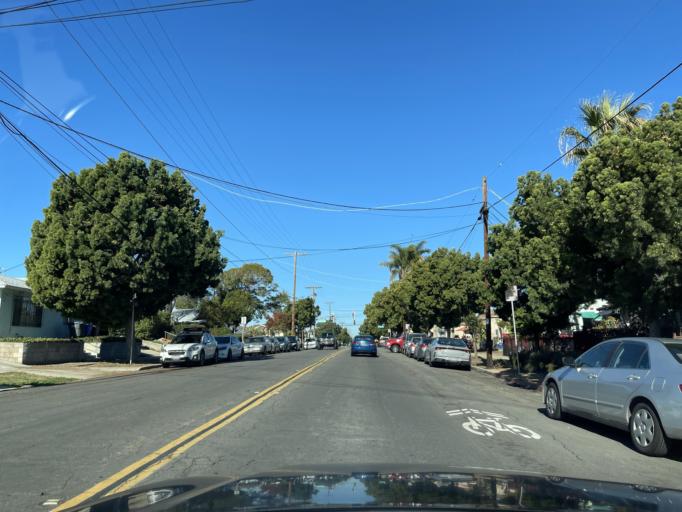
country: US
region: California
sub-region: San Diego County
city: National City
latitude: 32.6742
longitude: -117.1017
